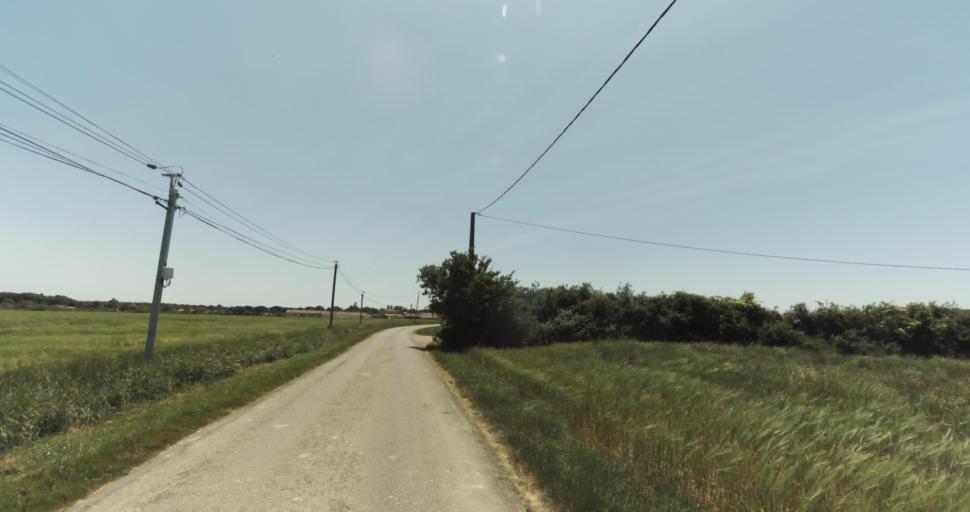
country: FR
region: Midi-Pyrenees
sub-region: Departement de la Haute-Garonne
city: Levignac
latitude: 43.6409
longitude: 1.1902
